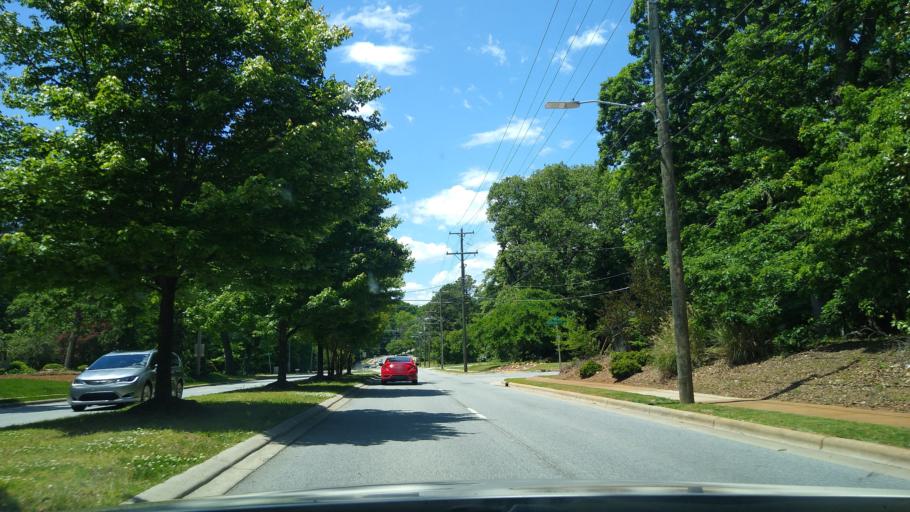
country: US
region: North Carolina
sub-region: Guilford County
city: Greensboro
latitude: 36.0911
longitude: -79.8619
